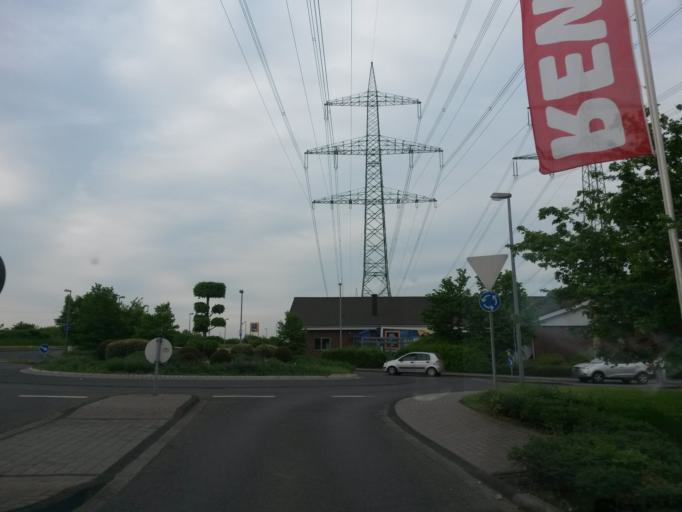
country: DE
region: North Rhine-Westphalia
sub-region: Regierungsbezirk Koln
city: Alfter
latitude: 50.7163
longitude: 7.0260
